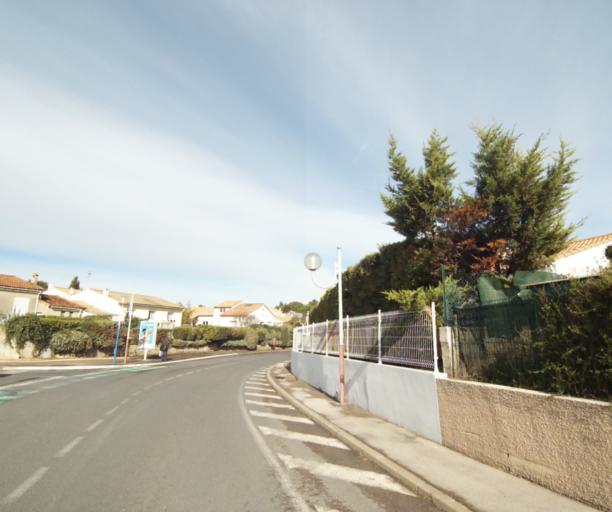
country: FR
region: Languedoc-Roussillon
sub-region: Departement de l'Herault
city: Saint-Jean-de-Vedas
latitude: 43.5800
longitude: 3.8223
